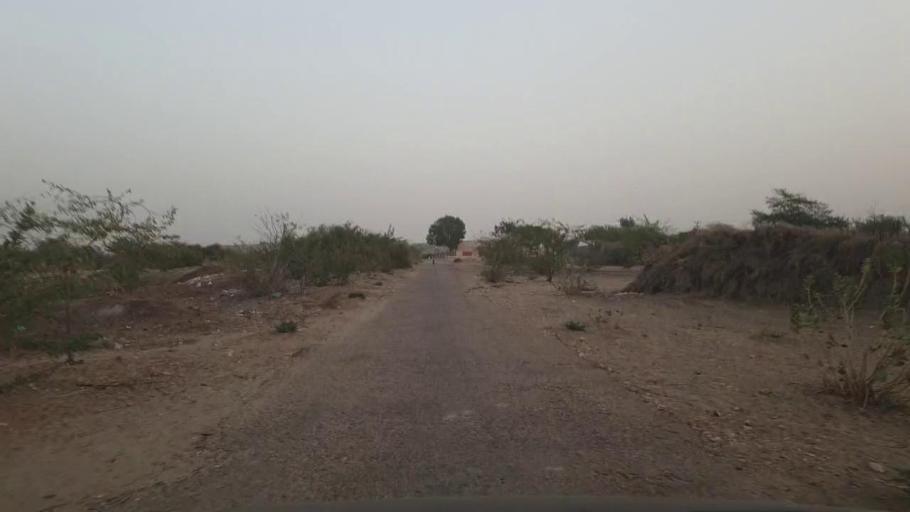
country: PK
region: Sindh
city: Chor
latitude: 25.5004
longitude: 69.8228
